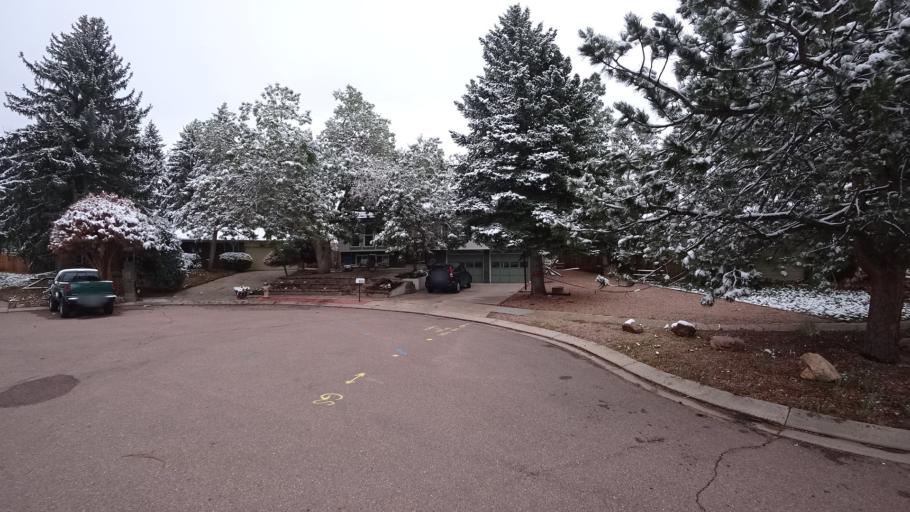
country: US
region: Colorado
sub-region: El Paso County
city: Colorado Springs
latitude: 38.8991
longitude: -104.7716
